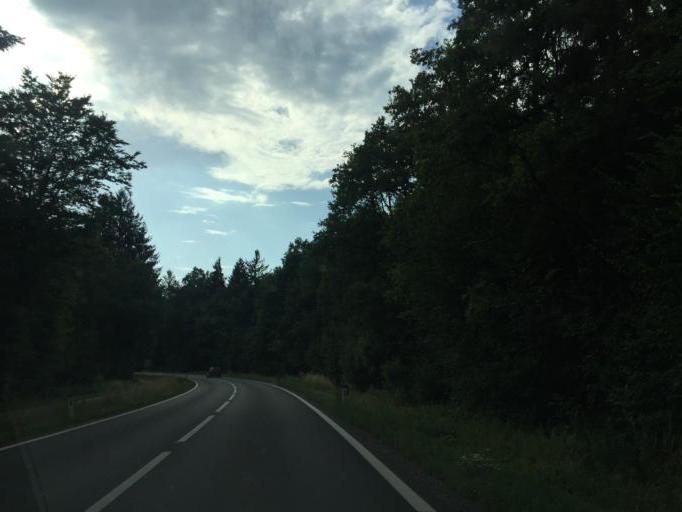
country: AT
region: Styria
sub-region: Politischer Bezirk Leibnitz
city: Sankt Veit am Vogau
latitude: 46.7571
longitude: 15.6349
